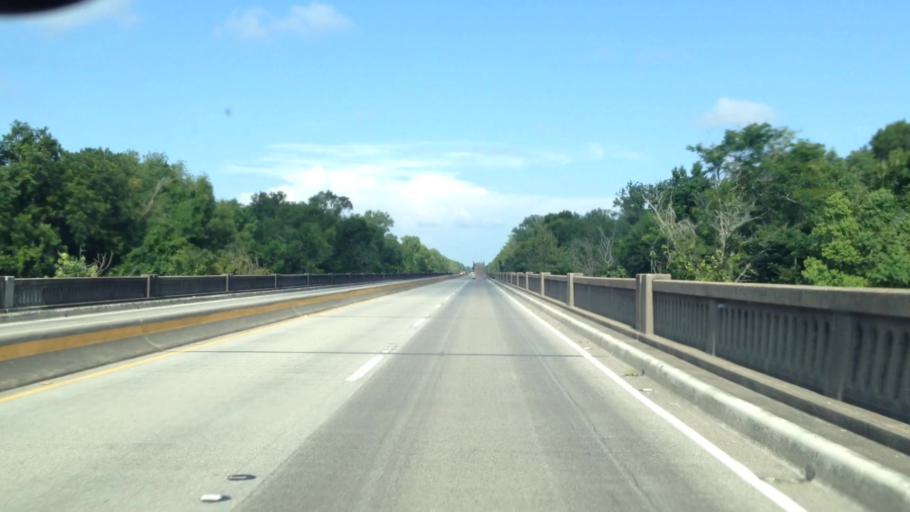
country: US
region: Louisiana
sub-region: Saint Landry Parish
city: Krotz Springs
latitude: 30.5541
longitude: -91.6964
